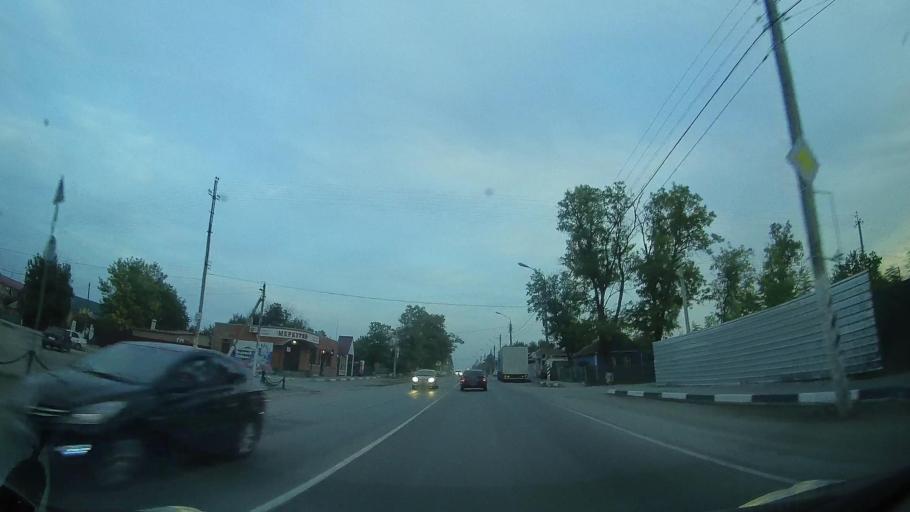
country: RU
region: Rostov
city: Kagal'nitskaya
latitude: 46.8810
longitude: 40.1508
